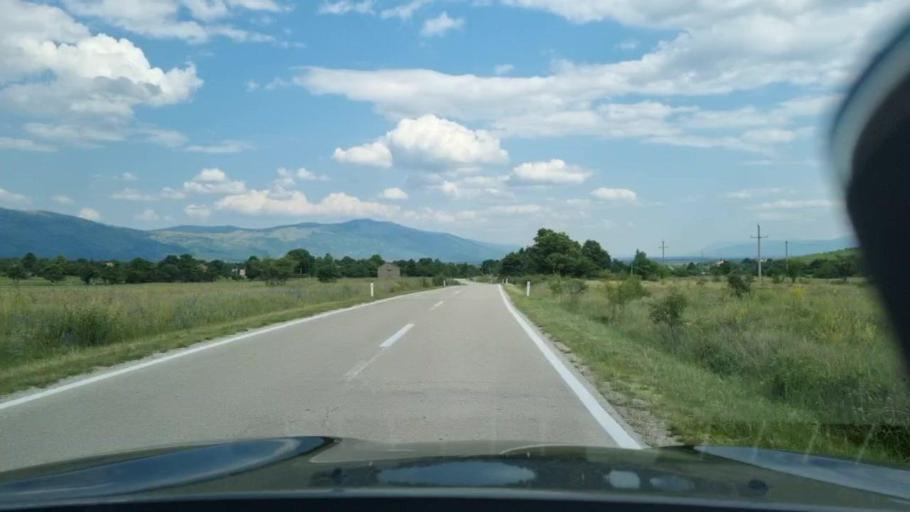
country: BA
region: Federation of Bosnia and Herzegovina
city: Bosansko Grahovo
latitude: 44.0944
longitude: 16.5585
